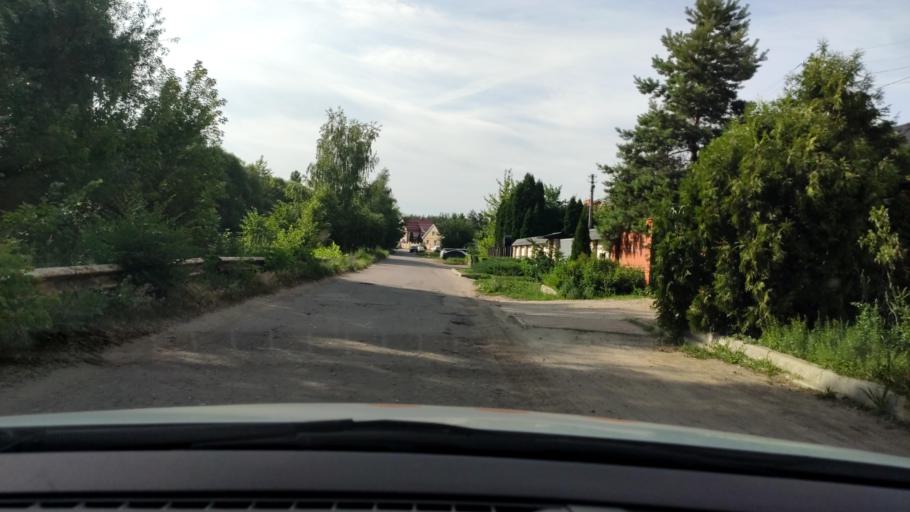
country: RU
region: Voronezj
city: Novaya Usman'
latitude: 51.6270
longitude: 39.4226
